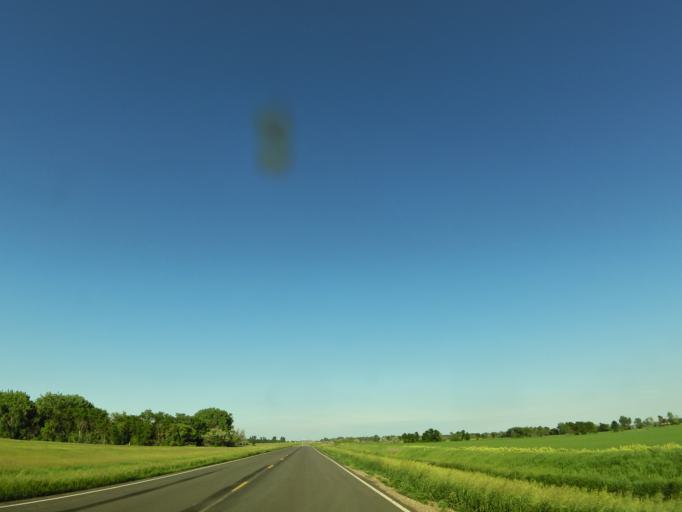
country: US
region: North Dakota
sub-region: Grand Forks County
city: Grand Forks Air Force Base
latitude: 48.1356
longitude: -97.2074
